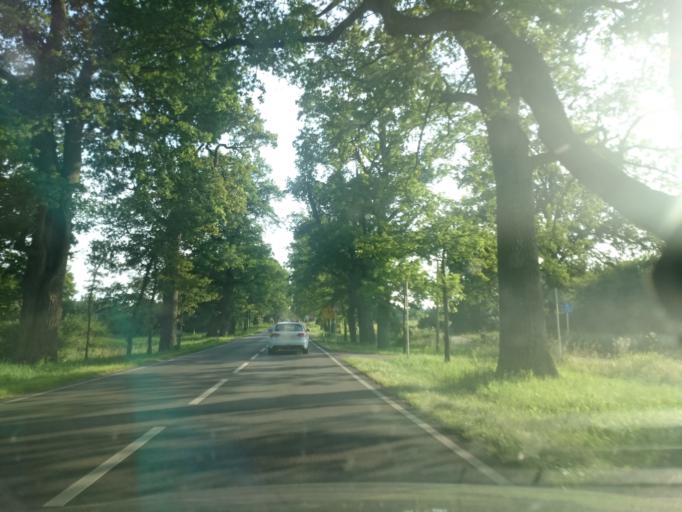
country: DE
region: Bavaria
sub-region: Upper Bavaria
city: Seefeld
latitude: 48.0451
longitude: 11.2159
